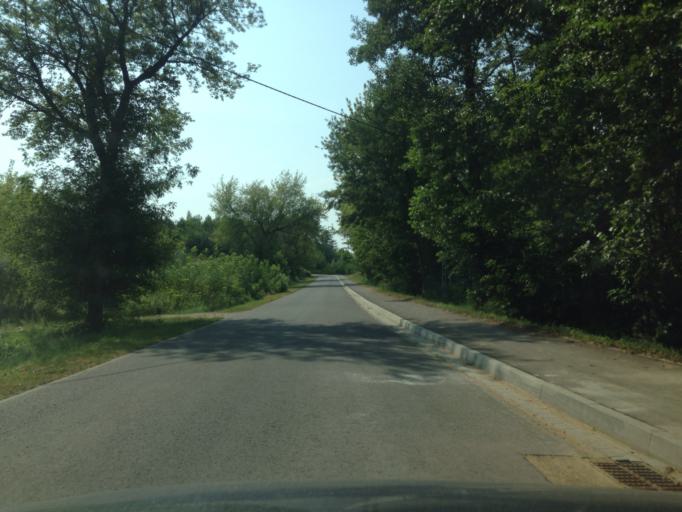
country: PL
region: Kujawsko-Pomorskie
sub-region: Powiat golubsko-dobrzynski
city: Golub-Dobrzyn
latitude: 53.0720
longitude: 19.0323
